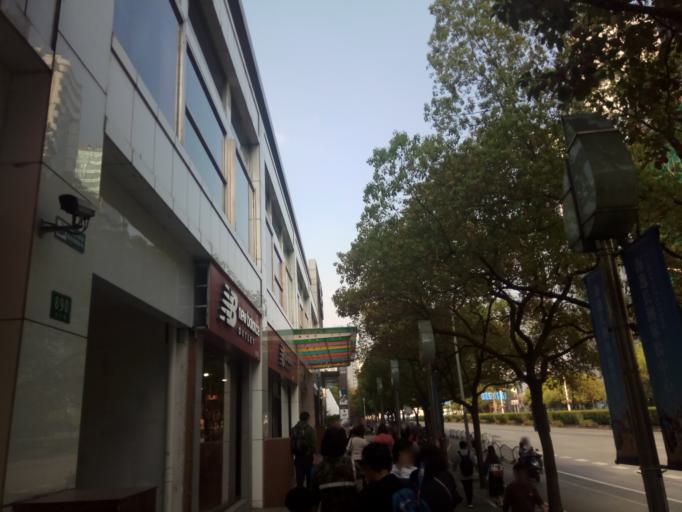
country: CN
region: Shanghai Shi
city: Changning
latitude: 31.2200
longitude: 121.4140
